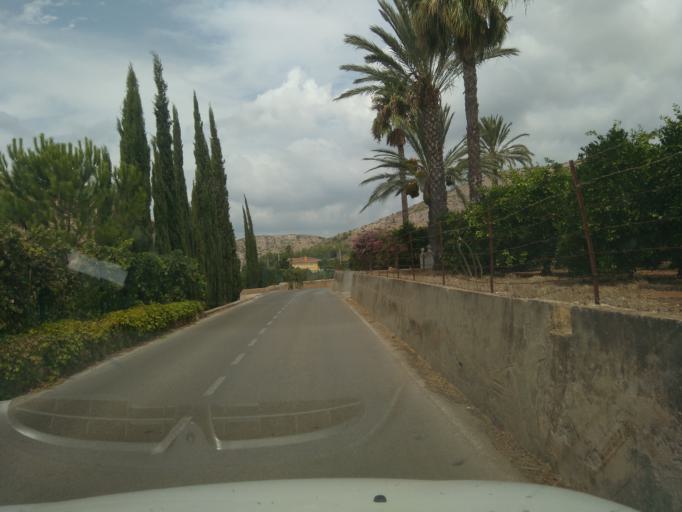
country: ES
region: Valencia
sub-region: Provincia de Valencia
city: La Pobla Llarga
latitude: 39.0823
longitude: -0.4239
